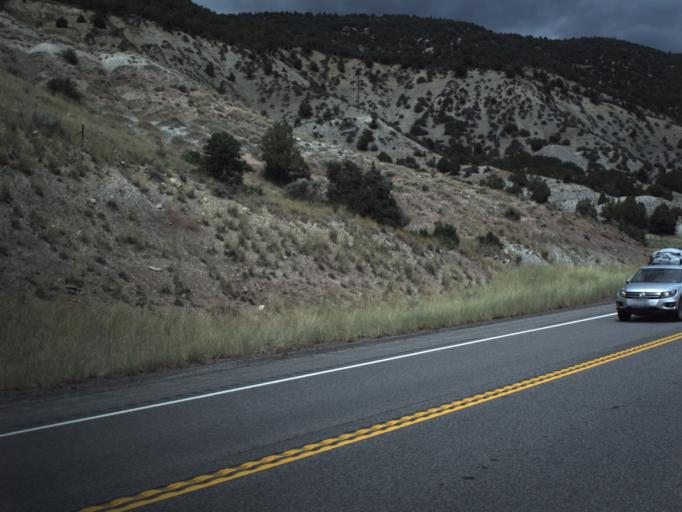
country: US
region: Utah
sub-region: Carbon County
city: Helper
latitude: 39.9337
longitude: -111.1520
